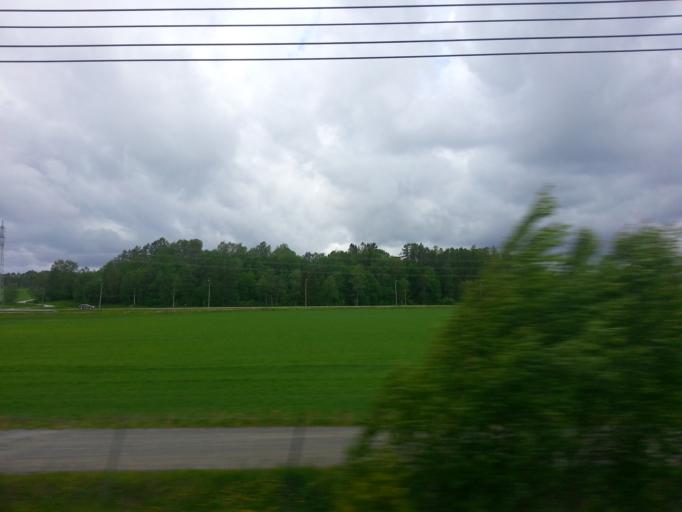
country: NO
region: Akershus
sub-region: Skedsmo
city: Leirsund
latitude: 59.9812
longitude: 11.0733
